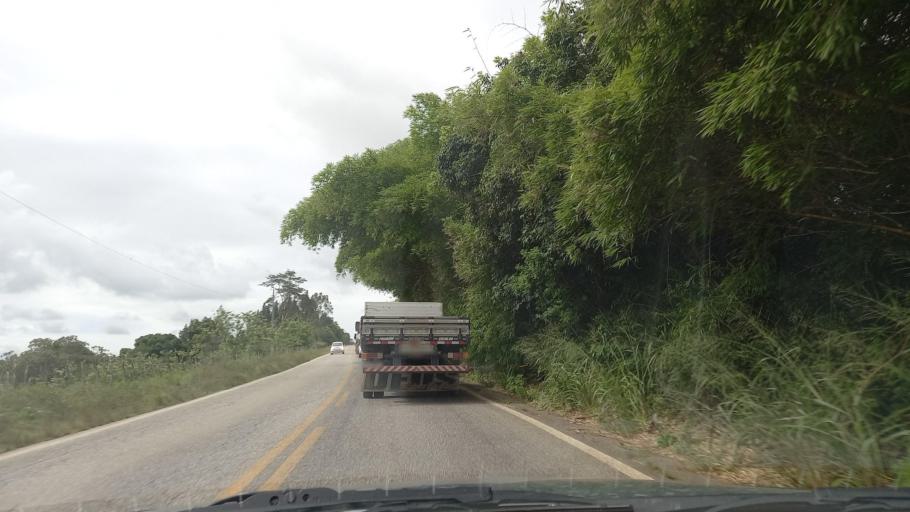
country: BR
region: Pernambuco
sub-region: Canhotinho
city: Canhotinho
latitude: -8.8634
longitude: -36.1824
